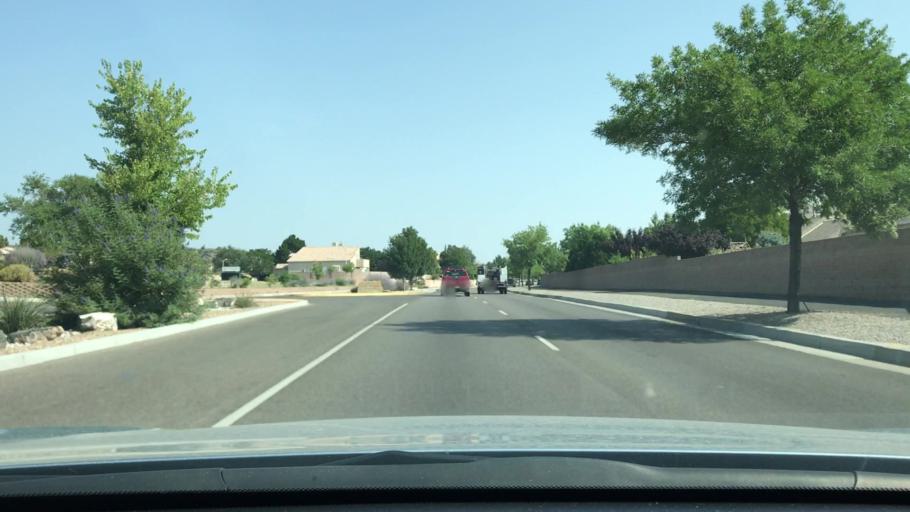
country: US
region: New Mexico
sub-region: Bernalillo County
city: Paradise Hills
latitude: 35.1821
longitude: -106.6873
